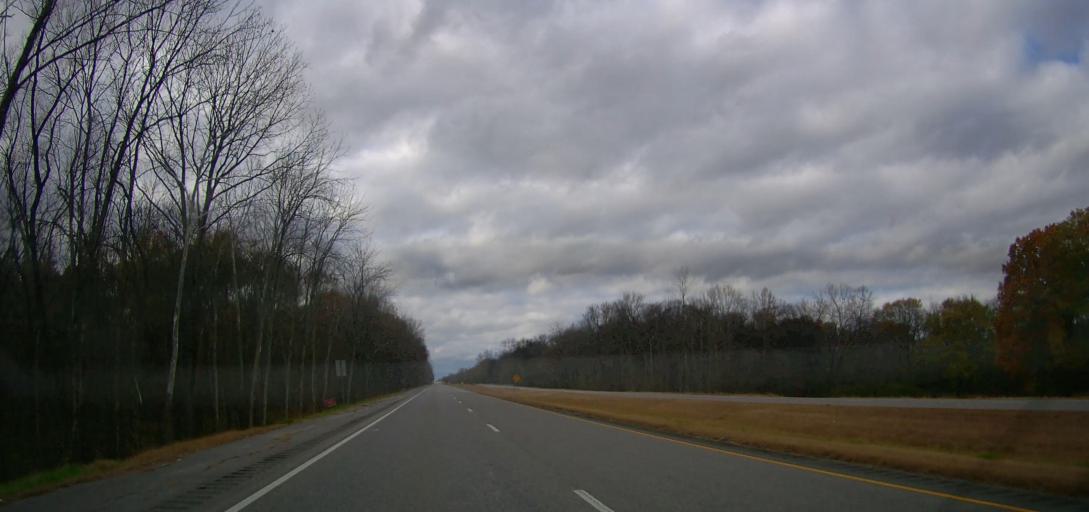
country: US
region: Alabama
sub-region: Lawrence County
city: Town Creek
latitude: 34.6296
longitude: -87.4826
